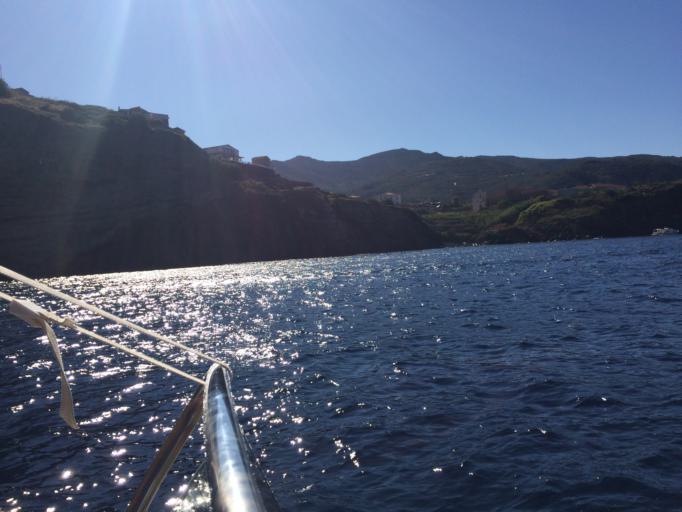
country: IT
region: Tuscany
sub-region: Provincia di Livorno
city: Capraia Isola
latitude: 43.0493
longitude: 9.8476
